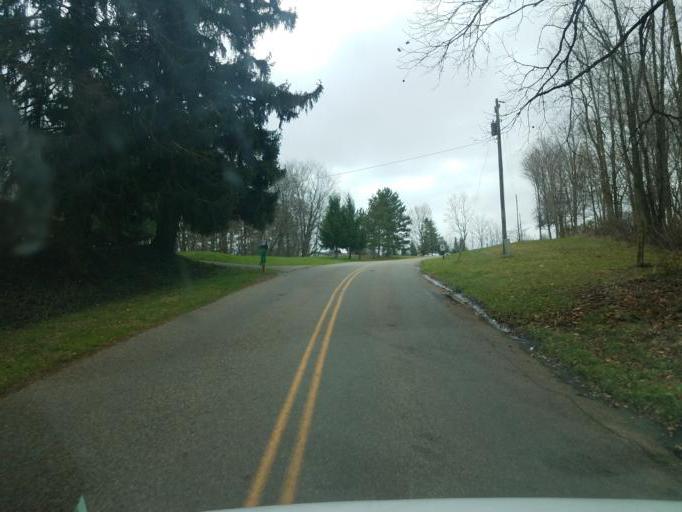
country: US
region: Ohio
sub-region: Knox County
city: Centerburg
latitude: 40.3443
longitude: -82.6280
